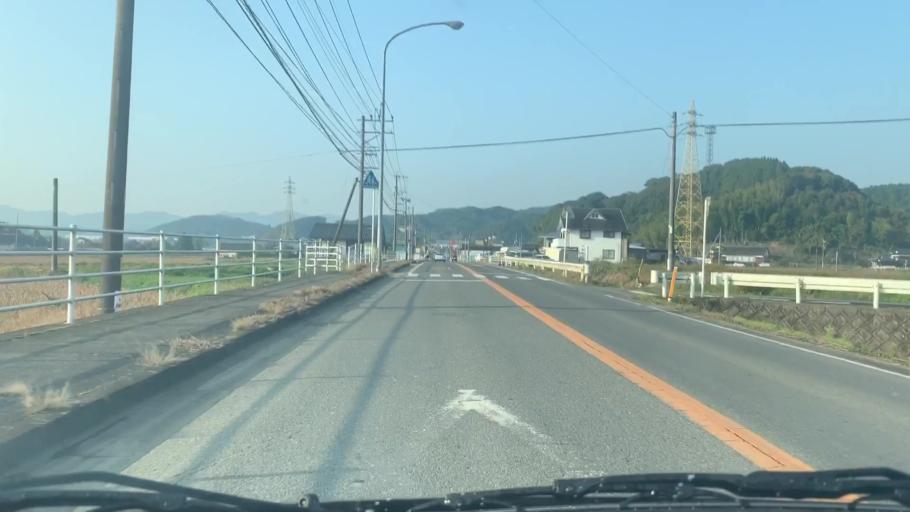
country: JP
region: Saga Prefecture
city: Takeocho-takeo
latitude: 33.1651
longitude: 130.0067
